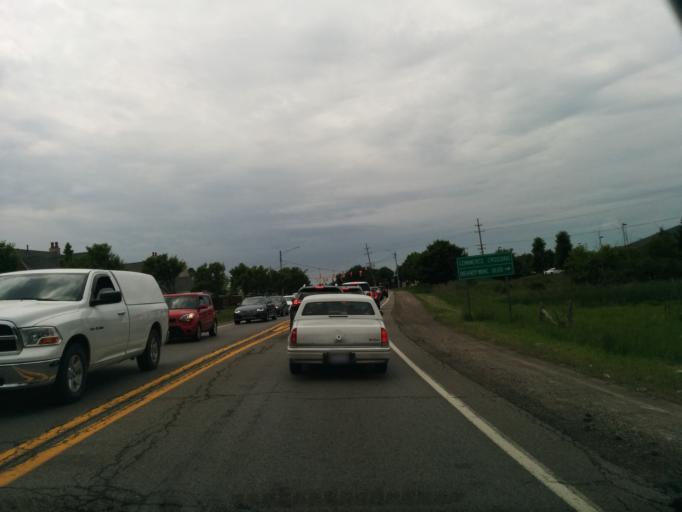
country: US
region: Michigan
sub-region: Oakland County
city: Wolverine Lake
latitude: 42.5370
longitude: -83.4367
